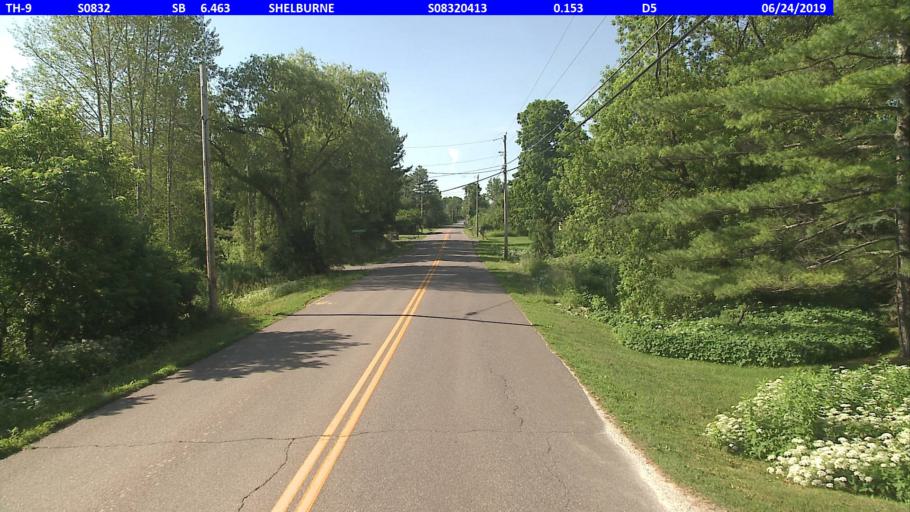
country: US
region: Vermont
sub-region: Chittenden County
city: Hinesburg
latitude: 44.3577
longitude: -73.2214
